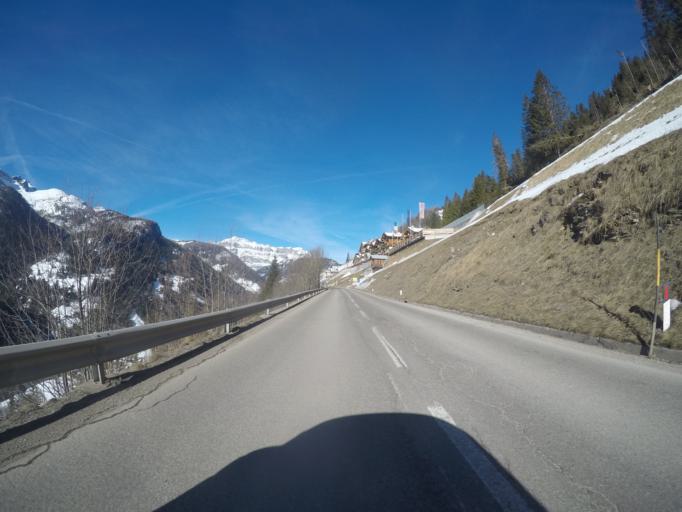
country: IT
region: Veneto
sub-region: Provincia di Belluno
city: Livinallongo del Col di Lana
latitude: 46.4789
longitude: 11.9597
